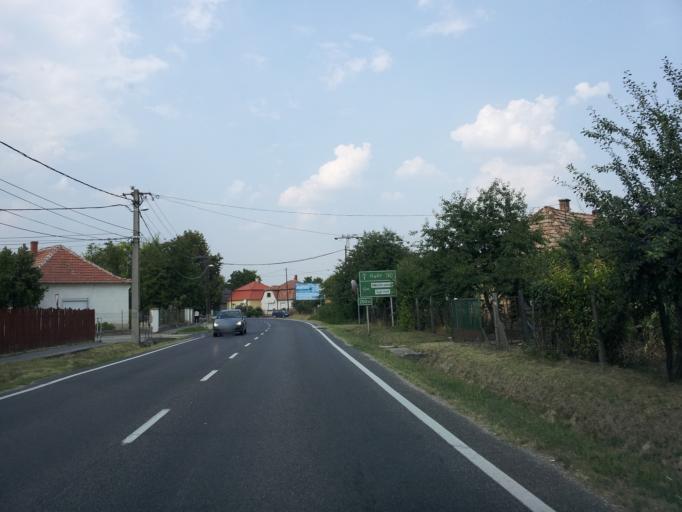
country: HU
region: Gyor-Moson-Sopron
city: Nyul
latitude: 47.5822
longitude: 17.6959
